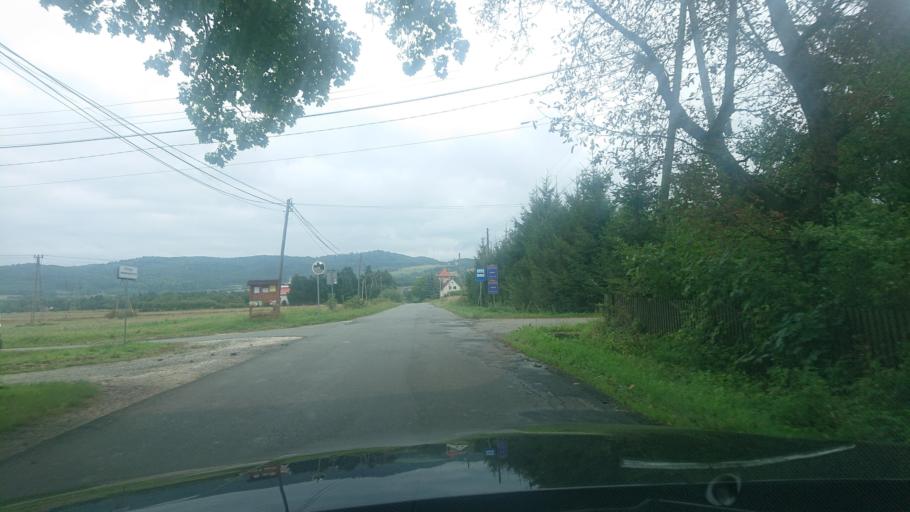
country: PL
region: Lower Silesian Voivodeship
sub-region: Powiat klodzki
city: Bystrzyca Klodzka
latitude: 50.3126
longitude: 16.6744
